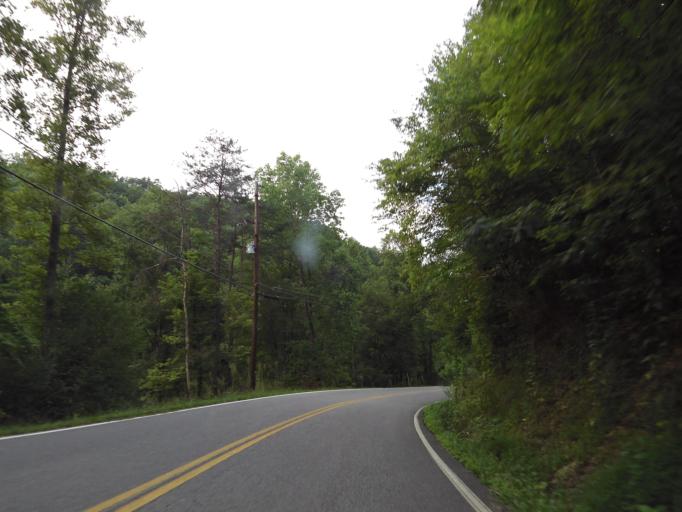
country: US
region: Tennessee
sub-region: Anderson County
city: Rocky Top
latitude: 36.1624
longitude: -84.1937
